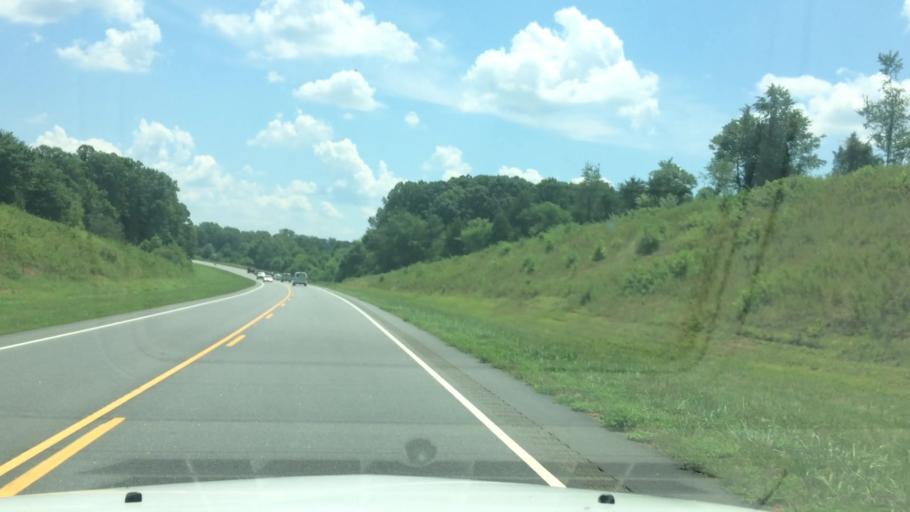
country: US
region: North Carolina
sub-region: Alexander County
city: Stony Point
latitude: 35.8649
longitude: -81.0605
